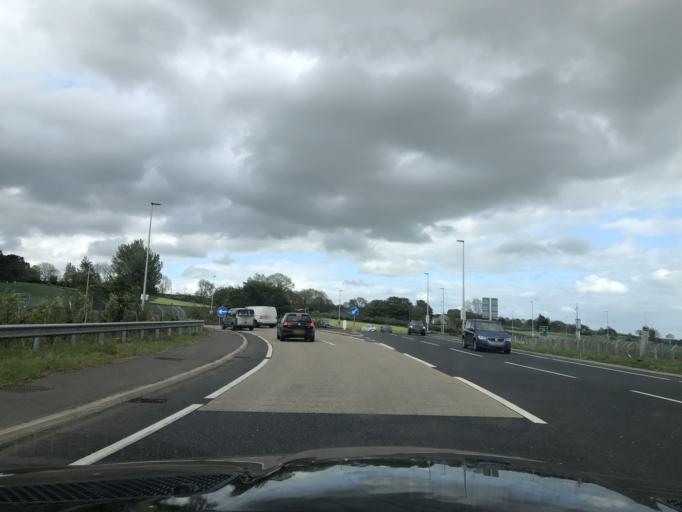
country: GB
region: Northern Ireland
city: Dunloy
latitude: 55.0167
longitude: -6.3688
